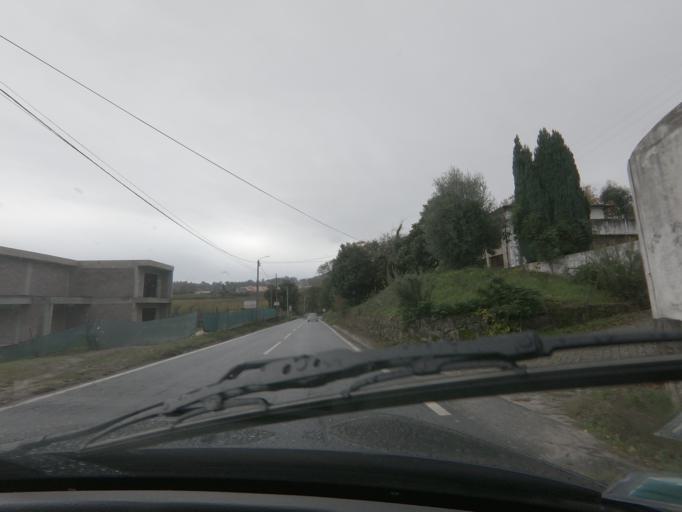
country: PT
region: Braga
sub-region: Celorico de Basto
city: Celorico de Basto
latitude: 41.4191
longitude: -7.9899
